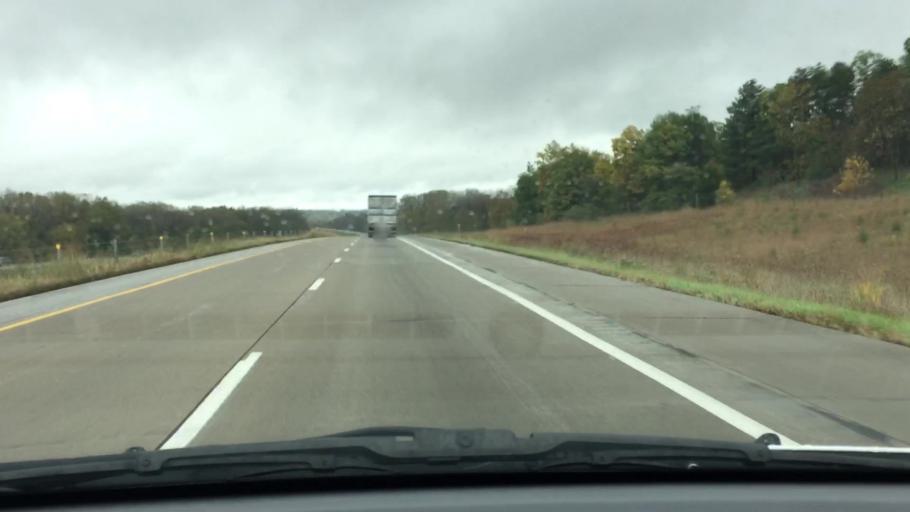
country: US
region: Iowa
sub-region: Jasper County
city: Colfax
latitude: 41.6865
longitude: -93.2776
